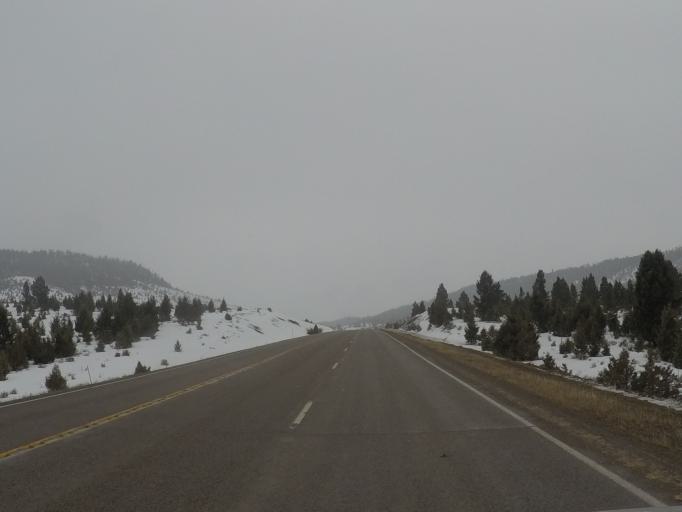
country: US
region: Montana
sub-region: Meagher County
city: White Sulphur Springs
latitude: 46.6610
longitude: -110.8741
